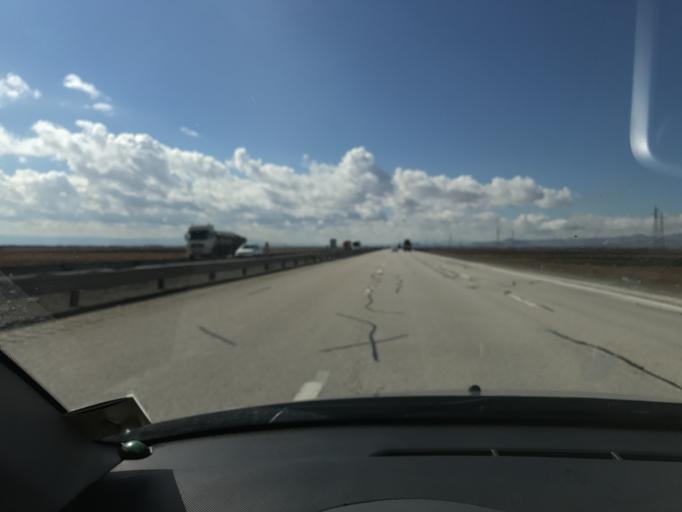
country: IR
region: Qazvin
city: Qazvin
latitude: 36.2196
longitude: 49.8818
